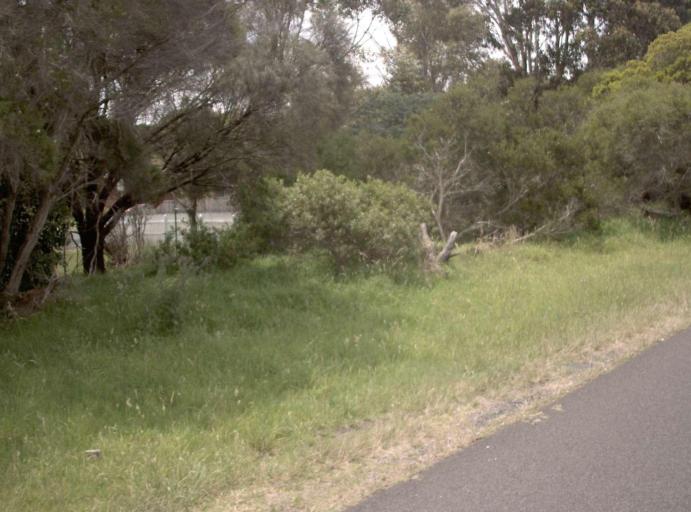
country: AU
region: Victoria
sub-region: Mornington Peninsula
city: McCrae
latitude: -38.3566
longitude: 144.9258
